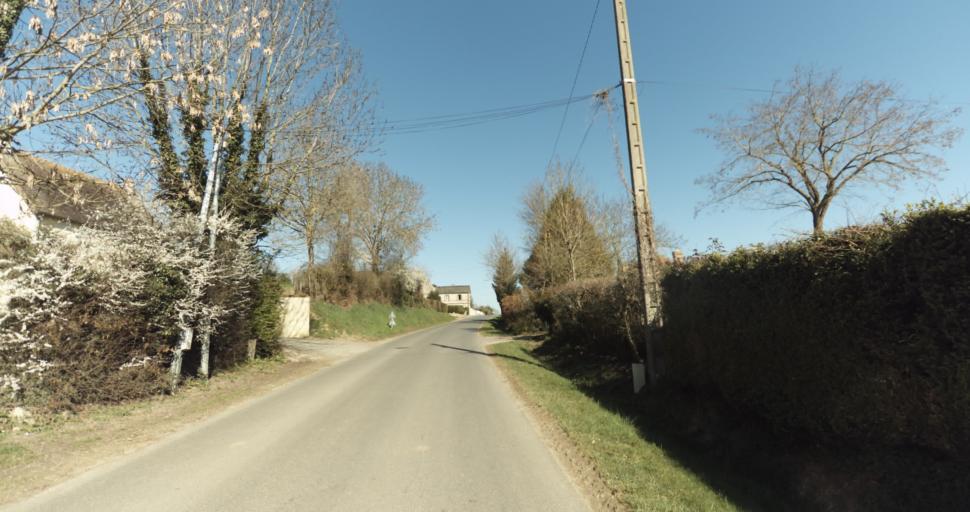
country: FR
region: Lower Normandy
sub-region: Departement du Calvados
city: Saint-Pierre-sur-Dives
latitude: 48.9757
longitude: 0.0370
